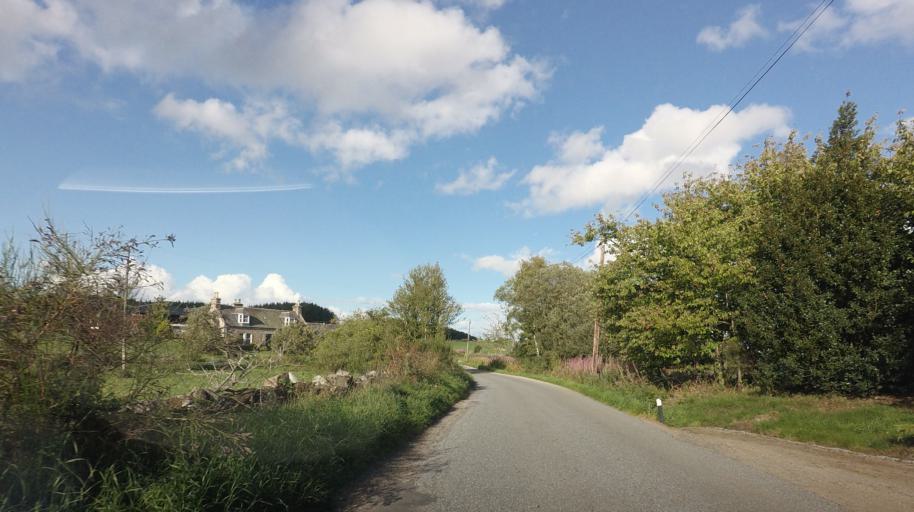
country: GB
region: Scotland
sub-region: Aberdeenshire
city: Banchory
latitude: 57.0750
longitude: -2.4621
